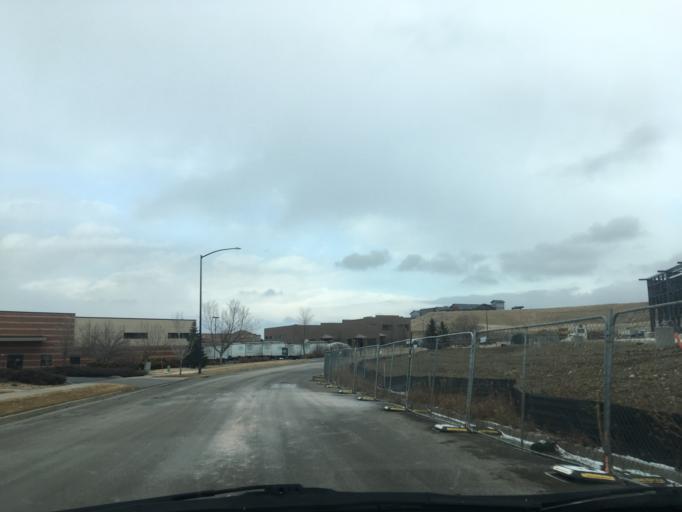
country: US
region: Colorado
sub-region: Boulder County
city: Lafayette
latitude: 39.9796
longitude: -105.0680
